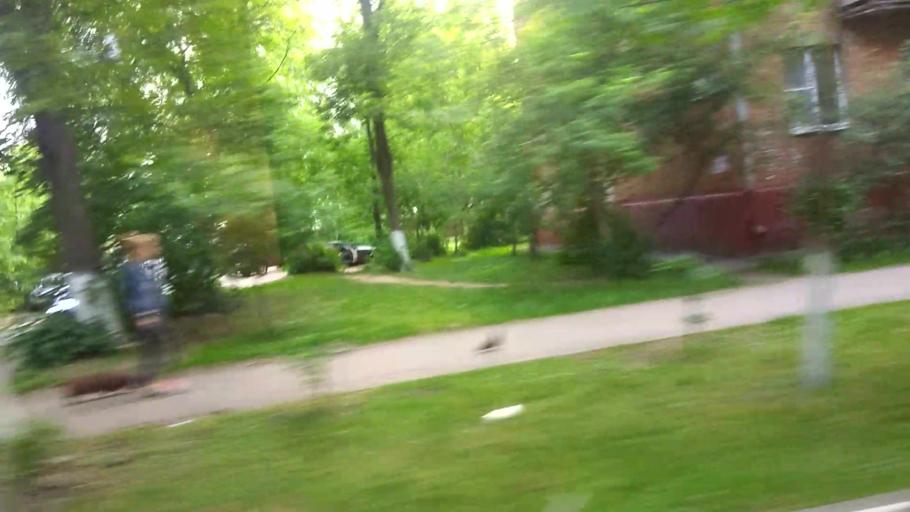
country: RU
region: Moskovskaya
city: Korolev
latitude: 55.9215
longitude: 37.8190
